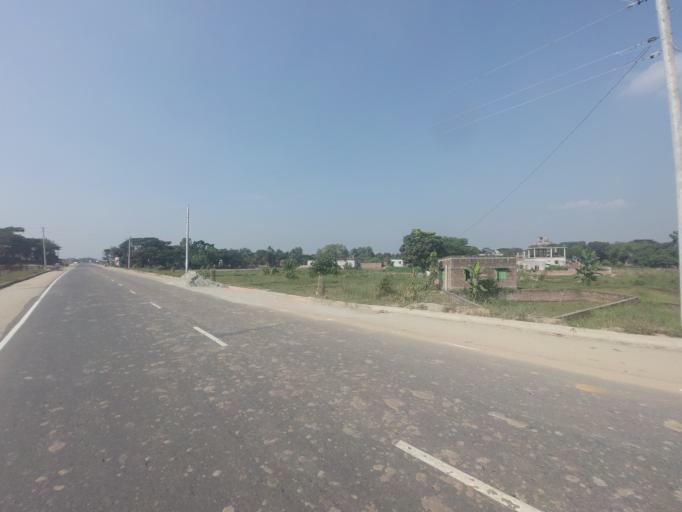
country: BD
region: Dhaka
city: Azimpur
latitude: 23.7344
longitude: 90.3316
